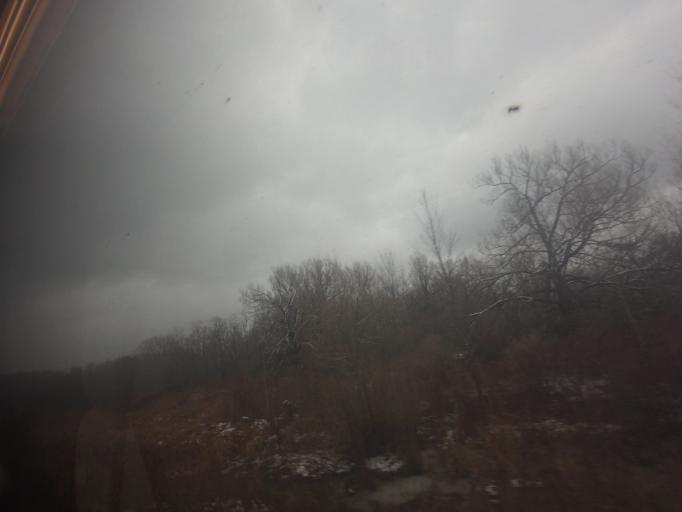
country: CA
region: Ontario
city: Cobourg
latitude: 43.9540
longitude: -78.2609
